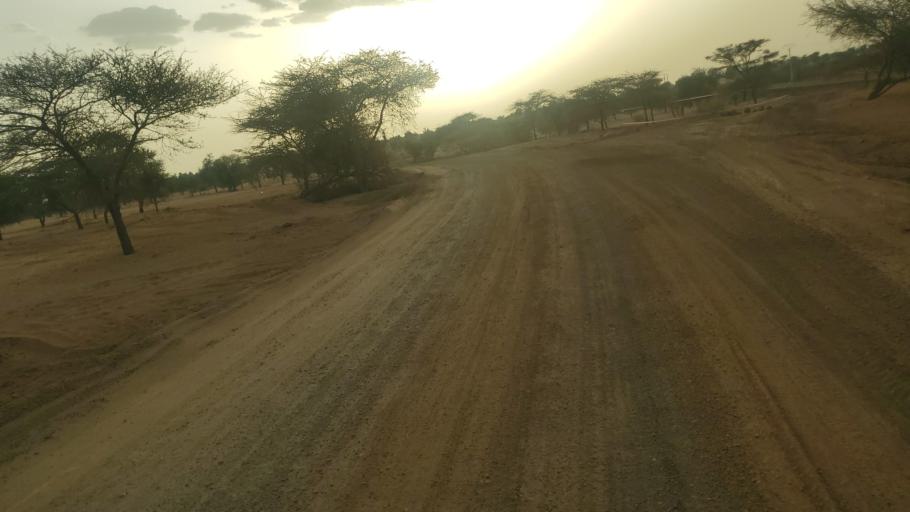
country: SN
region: Louga
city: Dara
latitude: 15.3746
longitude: -15.5866
